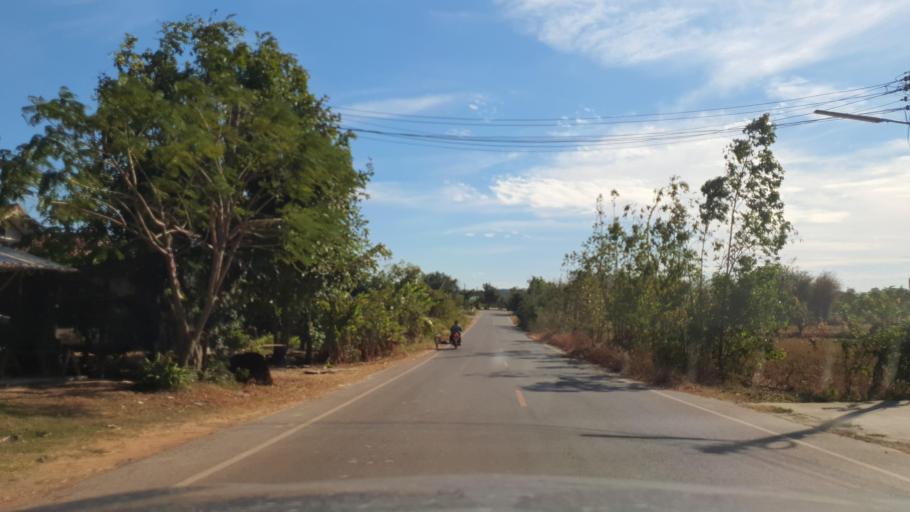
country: TH
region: Kalasin
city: Kuchinarai
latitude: 16.5975
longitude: 104.1348
